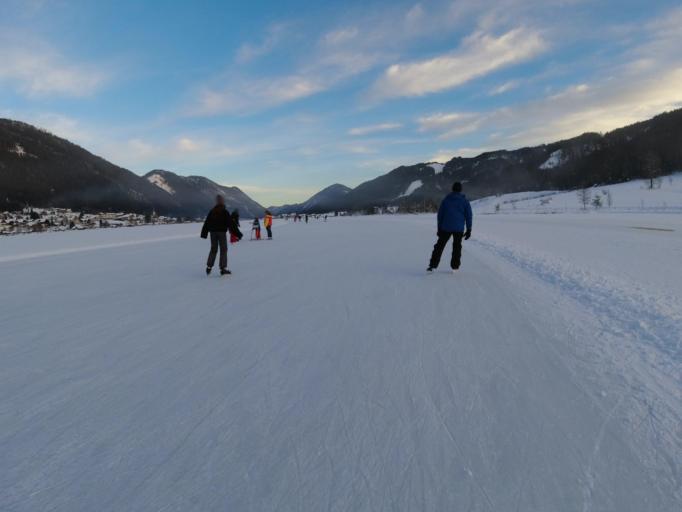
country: AT
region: Carinthia
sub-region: Politischer Bezirk Spittal an der Drau
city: Steinfeld
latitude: 46.7166
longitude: 13.2736
